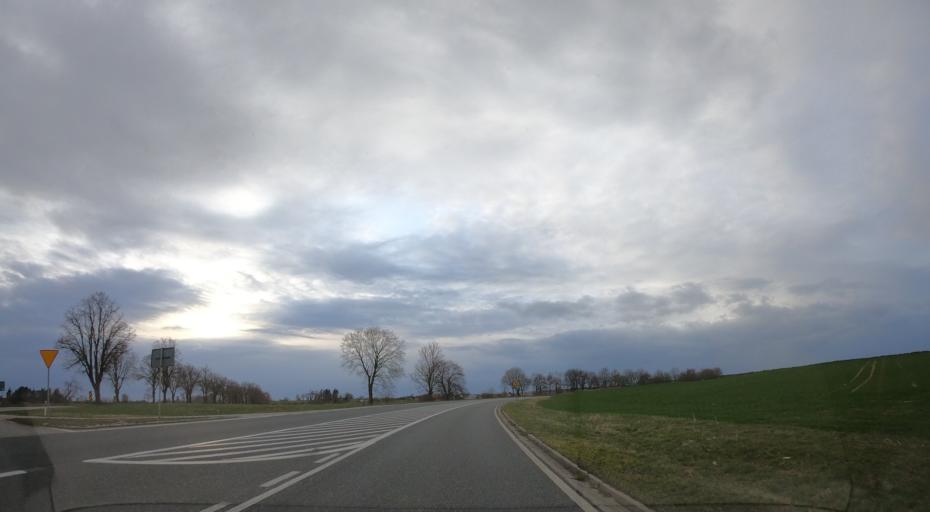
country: PL
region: West Pomeranian Voivodeship
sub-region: Powiat mysliborski
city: Nowogrodek Pomorski
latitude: 52.9040
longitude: 14.9758
